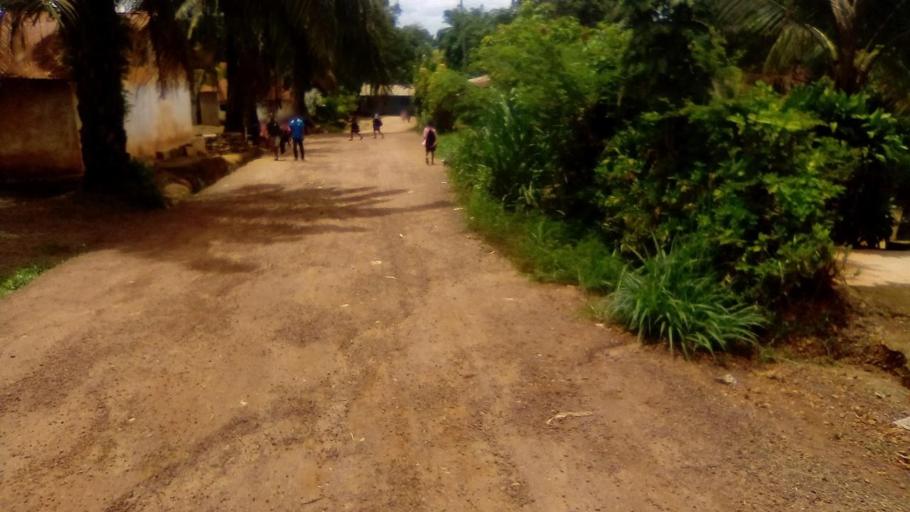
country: SL
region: Southern Province
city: Bo
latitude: 7.9379
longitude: -11.7340
